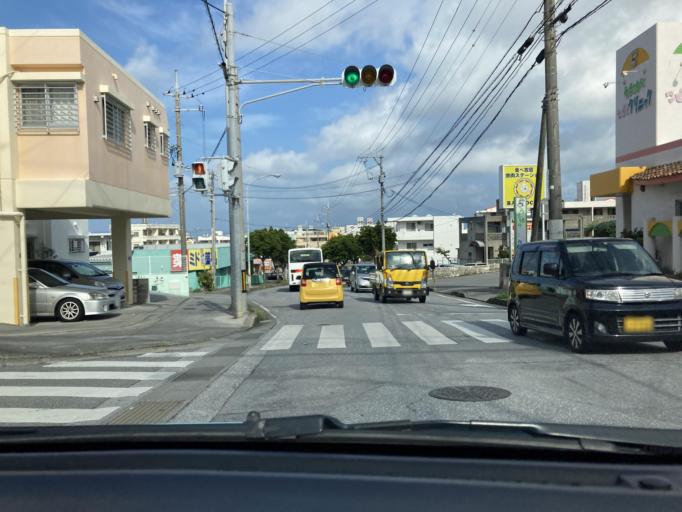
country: JP
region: Okinawa
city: Ginowan
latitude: 26.2610
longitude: 127.7635
